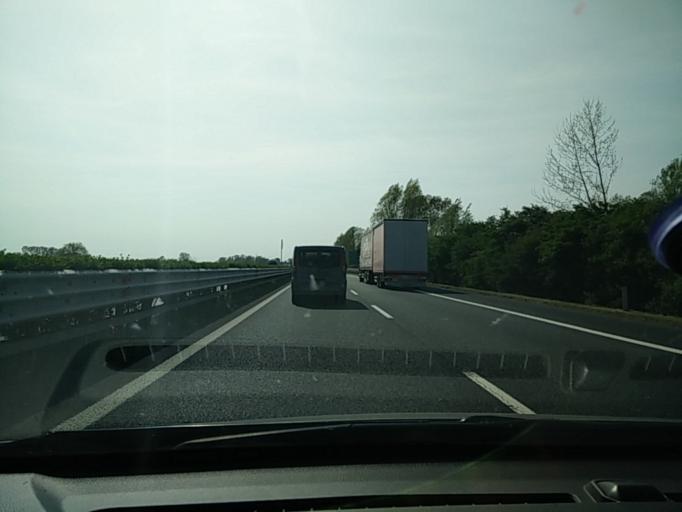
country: IT
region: Veneto
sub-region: Provincia di Venezia
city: Portogruaro
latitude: 45.7964
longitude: 12.8390
